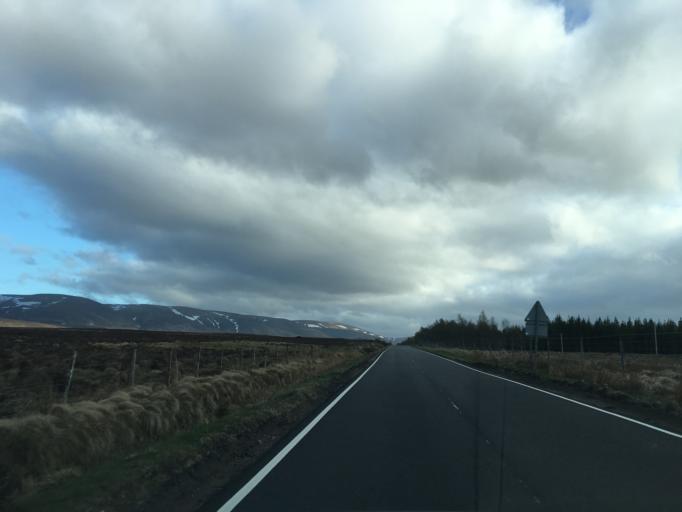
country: GB
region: Scotland
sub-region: Highland
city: Kingussie
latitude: 56.9548
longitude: -4.2444
